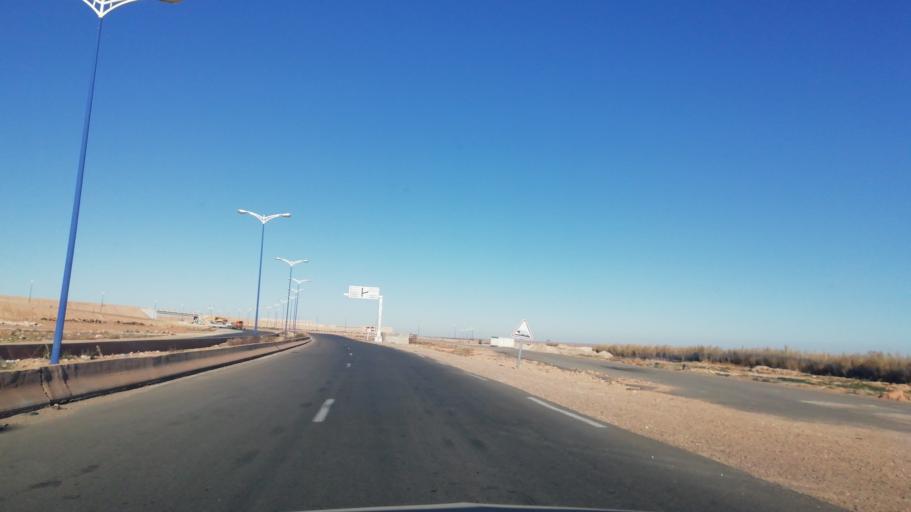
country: DZ
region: Wilaya de Naama
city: Naama
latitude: 33.5527
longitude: -0.2392
